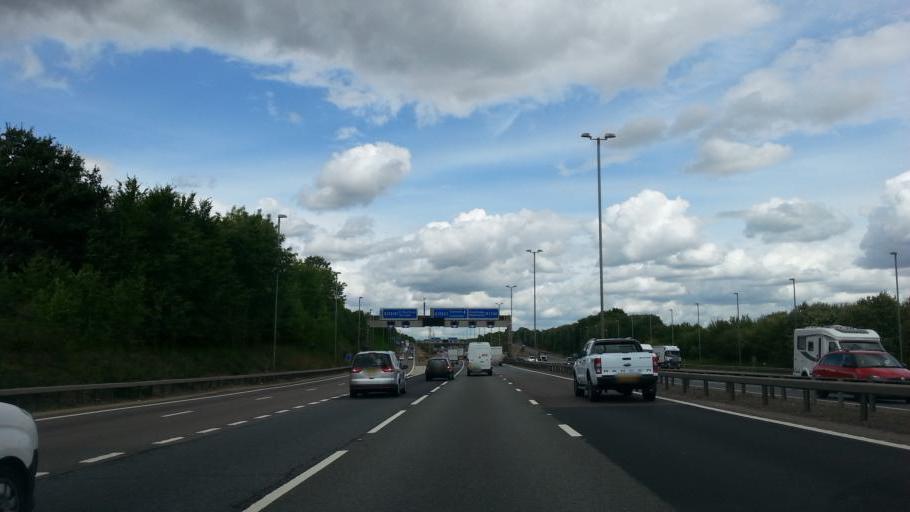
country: GB
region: England
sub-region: Essex
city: Little Hallingbury
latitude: 51.8651
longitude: 0.1942
